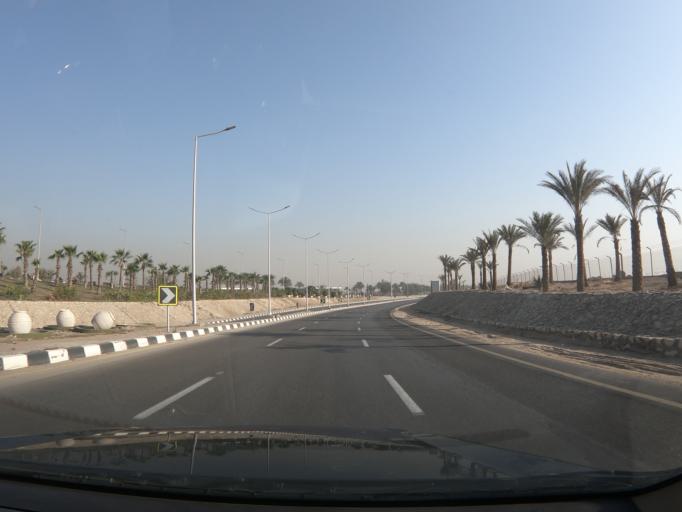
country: EG
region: Muhafazat al Qalyubiyah
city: Al Khankah
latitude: 30.0968
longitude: 31.3848
